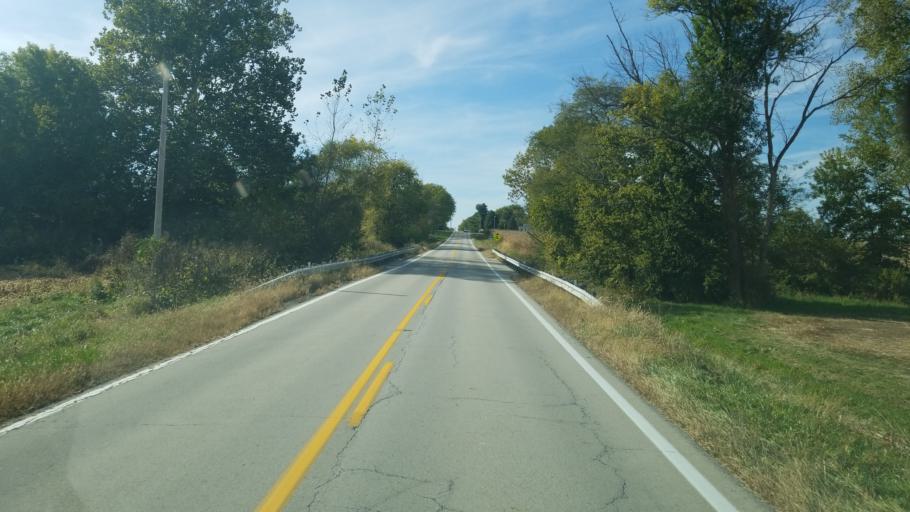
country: US
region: Ohio
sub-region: Clinton County
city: Wilmington
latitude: 39.3549
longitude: -83.7933
